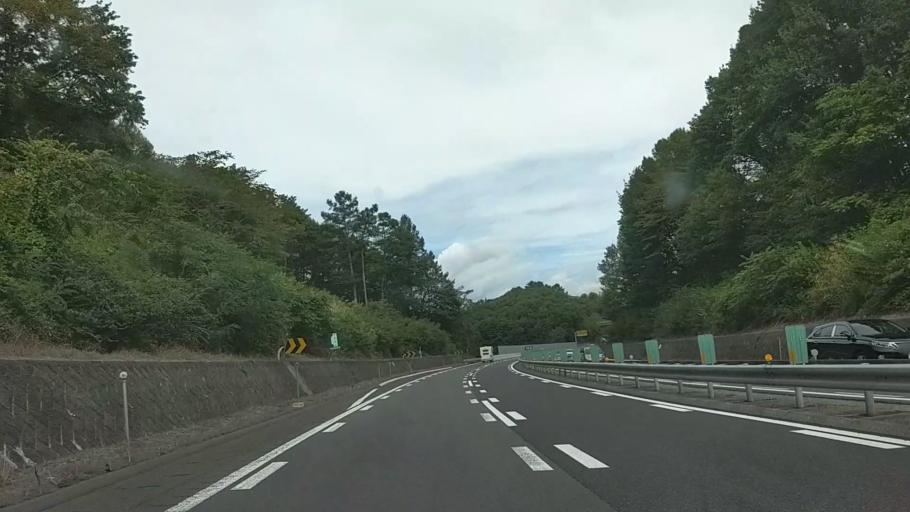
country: JP
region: Nagano
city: Chino
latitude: 35.9731
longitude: 138.1759
